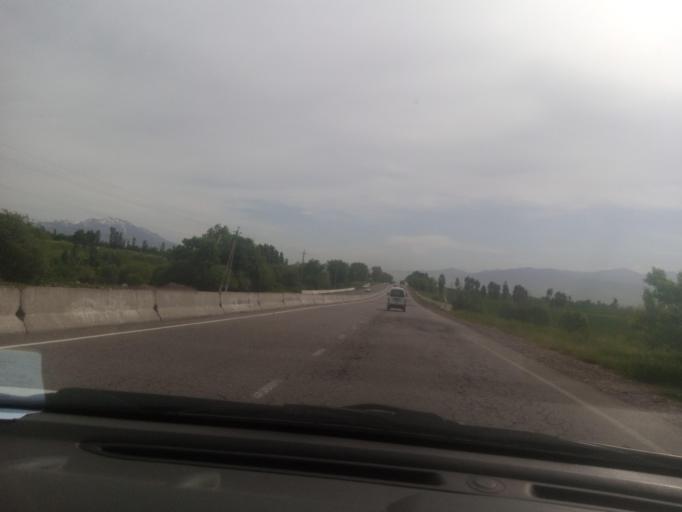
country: UZ
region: Toshkent
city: Angren
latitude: 40.9689
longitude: 69.9795
